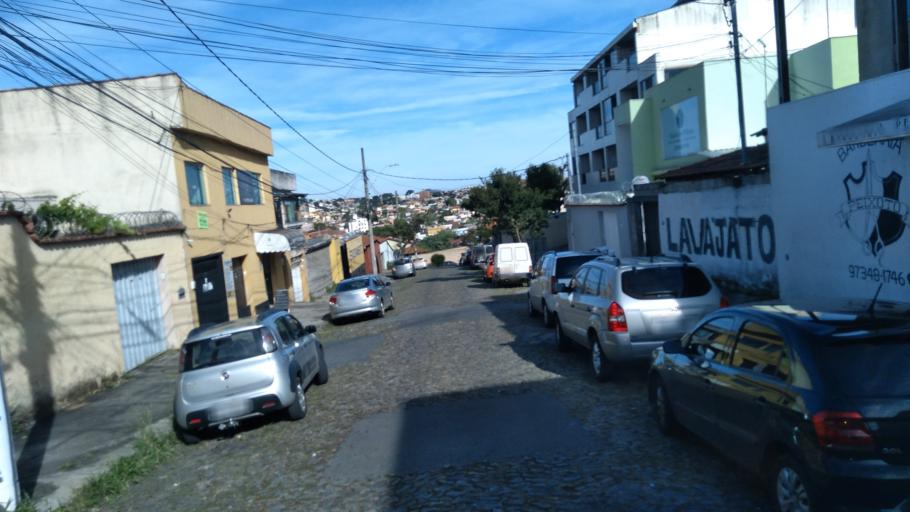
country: BR
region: Minas Gerais
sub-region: Contagem
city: Contagem
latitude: -19.9010
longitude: -44.0049
